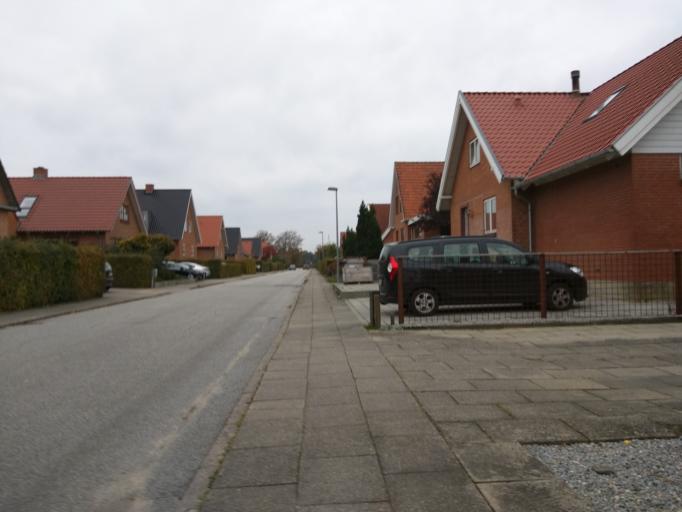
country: DK
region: Central Jutland
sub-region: Viborg Kommune
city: Viborg
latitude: 56.4562
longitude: 9.3869
